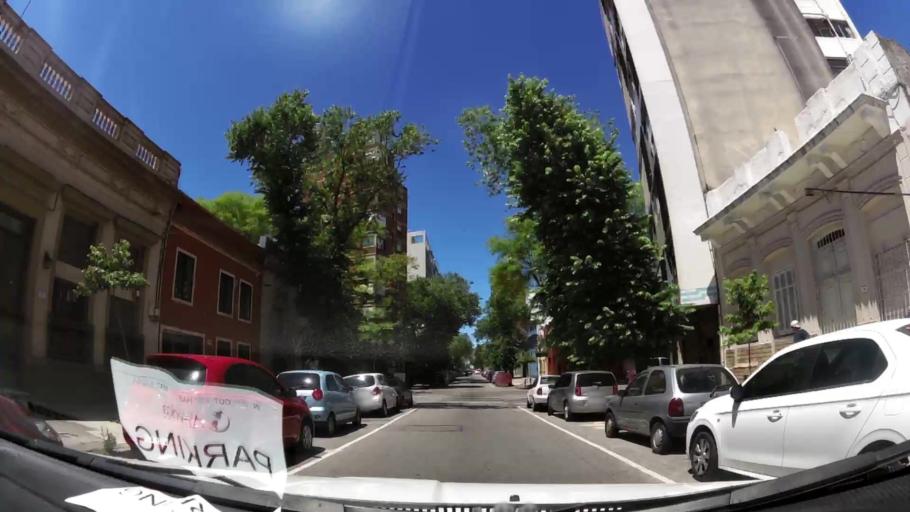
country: UY
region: Montevideo
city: Montevideo
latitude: -34.9059
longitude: -56.1745
